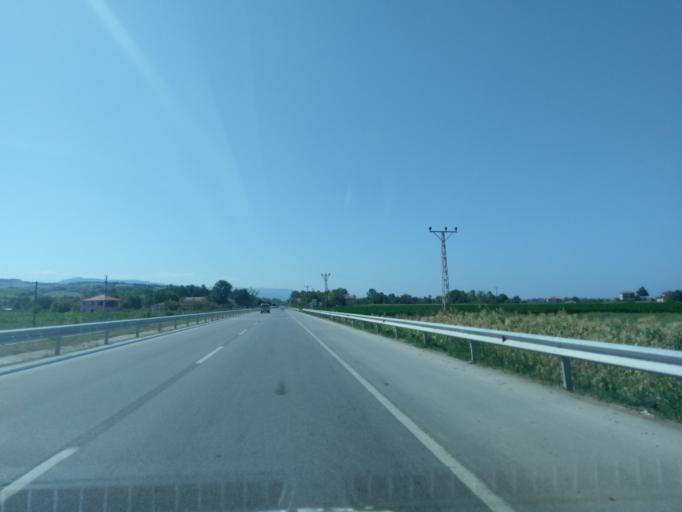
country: TR
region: Samsun
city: Alacam
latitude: 41.6096
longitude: 35.6561
